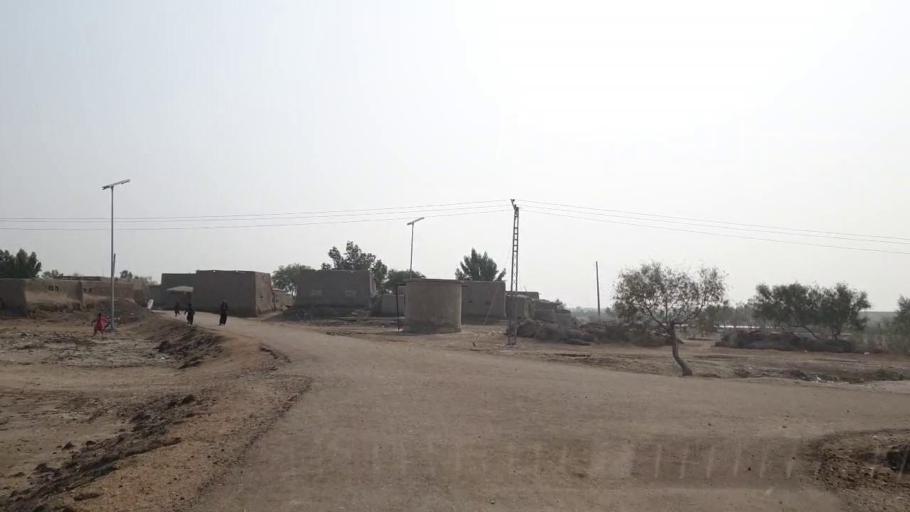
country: PK
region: Sindh
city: Bhan
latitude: 26.4565
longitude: 67.6942
